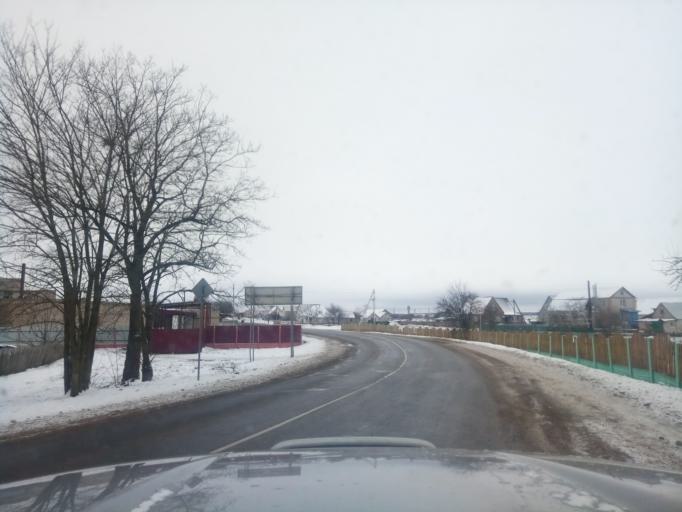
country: BY
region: Minsk
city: Kapyl'
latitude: 53.1616
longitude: 27.0858
